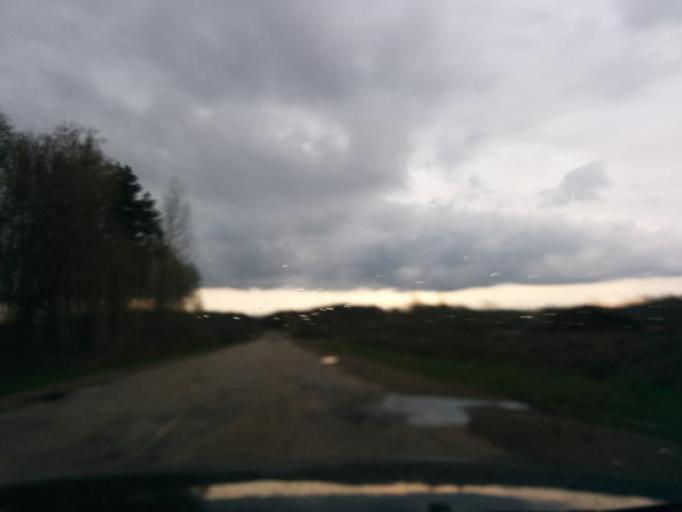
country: LT
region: Siauliu apskritis
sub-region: Joniskis
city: Joniskis
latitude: 56.4164
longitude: 23.6111
